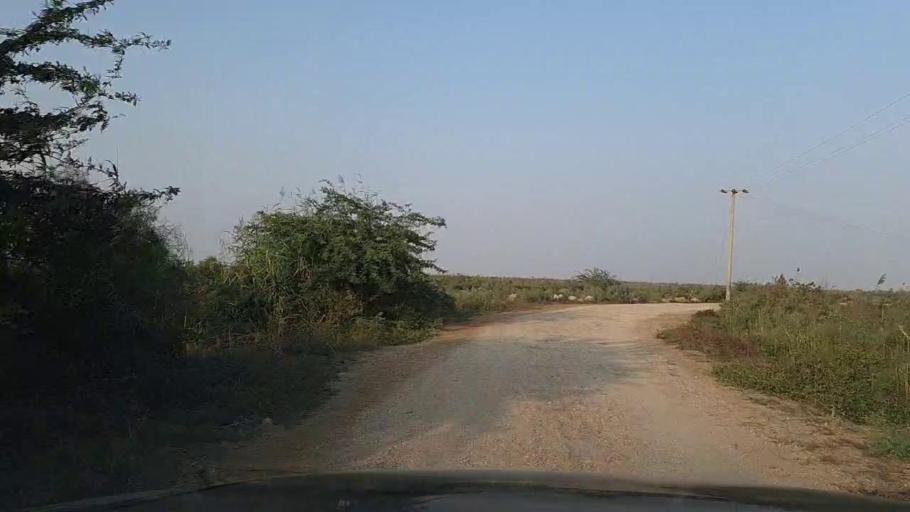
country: PK
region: Sindh
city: Mirpur Sakro
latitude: 24.4165
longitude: 67.7331
